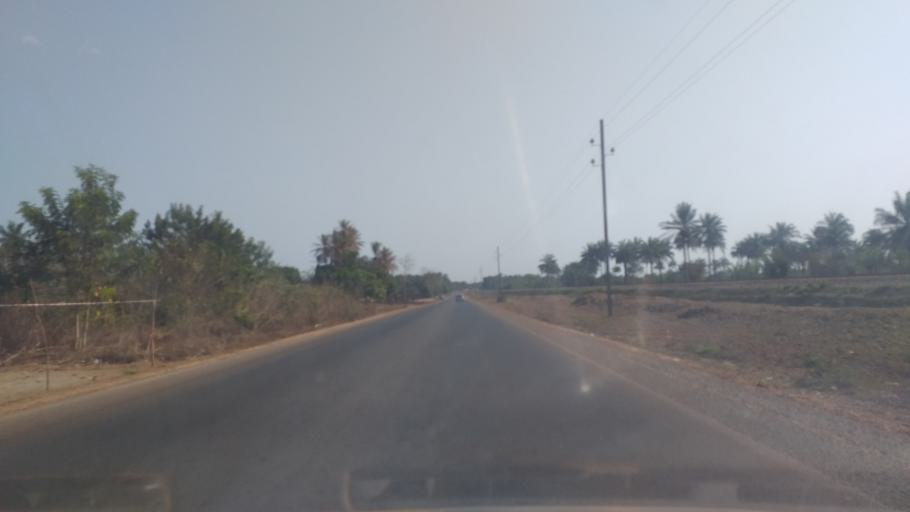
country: GN
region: Boke
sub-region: Boke Prefecture
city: Kamsar
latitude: 10.7272
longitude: -14.5187
